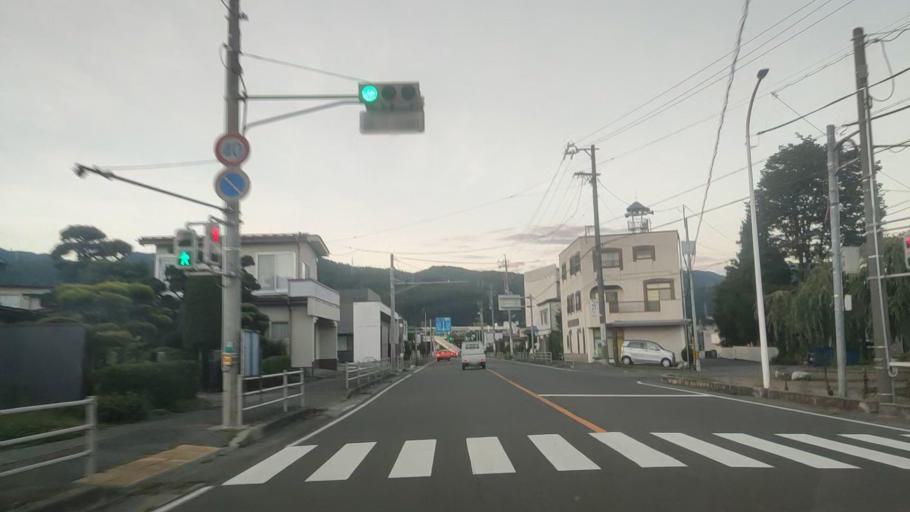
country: JP
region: Nagano
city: Okaya
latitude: 36.0771
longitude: 138.0652
